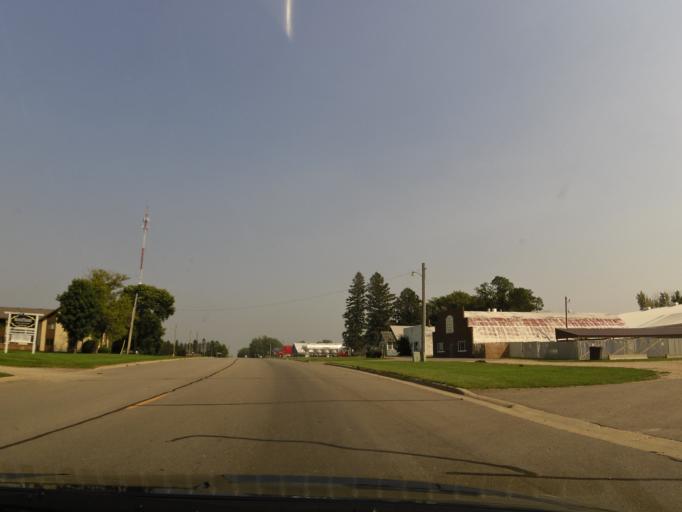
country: US
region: Minnesota
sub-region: Grant County
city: Elbow Lake
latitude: 45.9922
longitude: -95.9634
